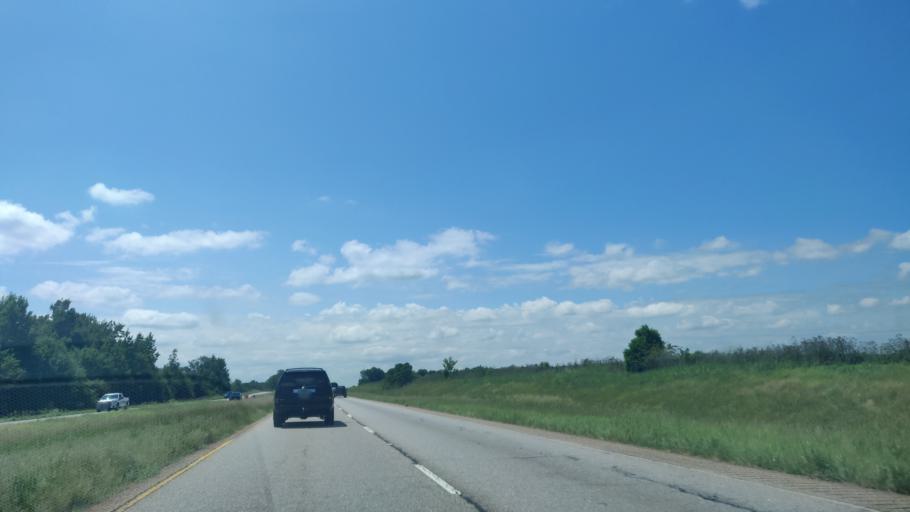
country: US
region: Georgia
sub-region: Stewart County
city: Richland
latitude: 32.0769
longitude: -84.6733
